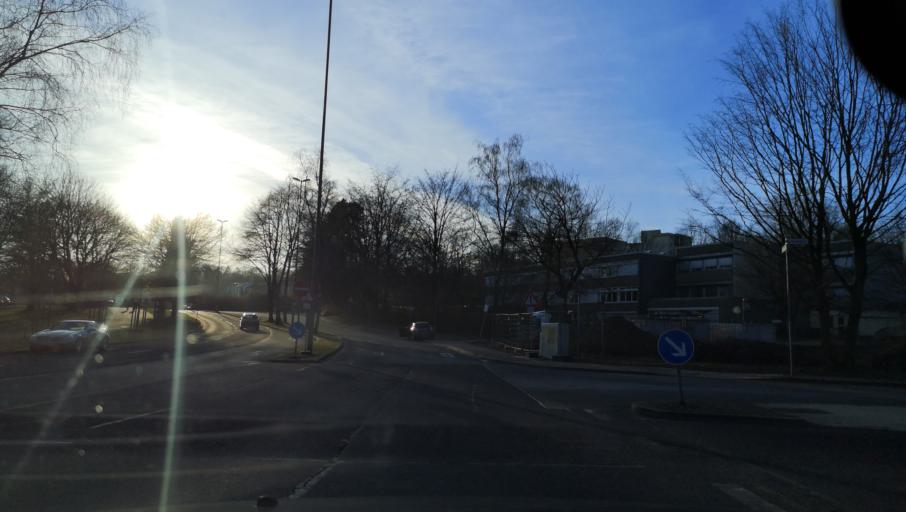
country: DE
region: North Rhine-Westphalia
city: Radevormwald
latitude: 51.2003
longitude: 7.2787
